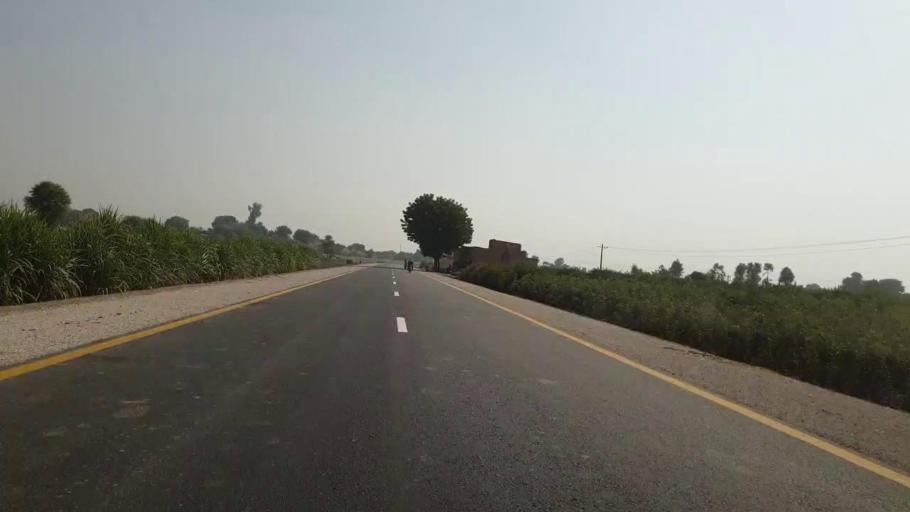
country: PK
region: Sindh
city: Bhan
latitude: 26.6055
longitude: 67.7792
